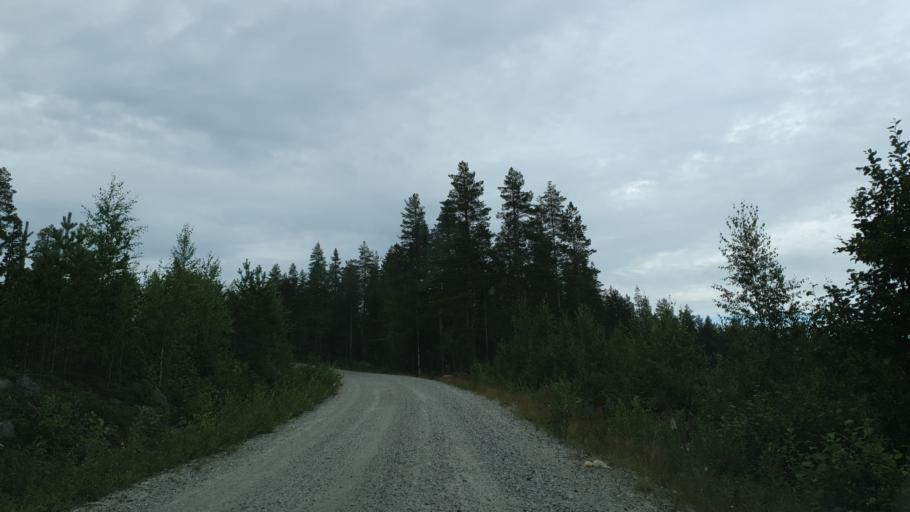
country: FI
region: Kainuu
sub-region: Kehys-Kainuu
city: Kuhmo
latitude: 64.4582
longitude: 29.5800
